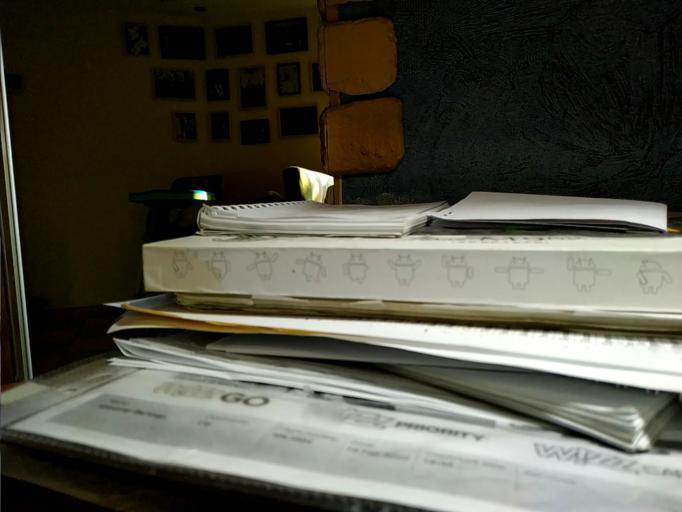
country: RU
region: Novgorod
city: Kholm
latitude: 57.0992
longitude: 31.5039
